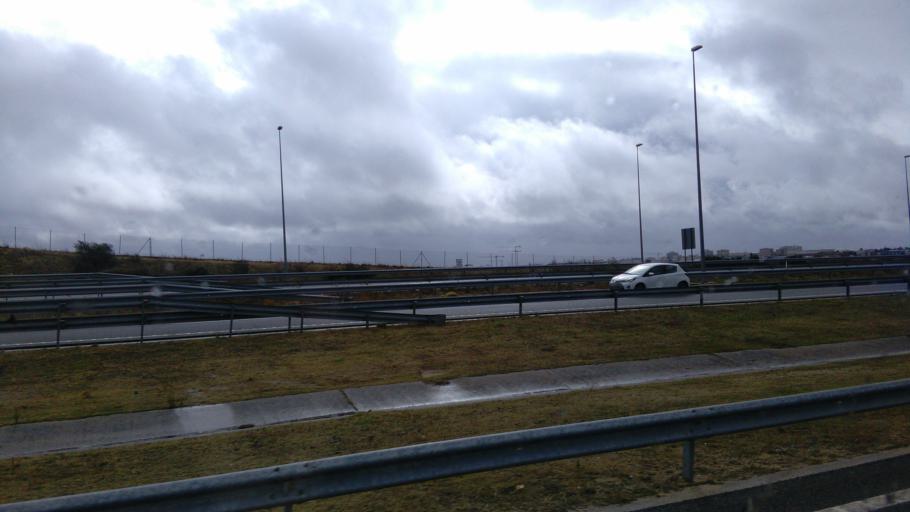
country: ES
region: Madrid
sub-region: Provincia de Madrid
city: Alcorcon
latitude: 40.3133
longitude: -3.8248
